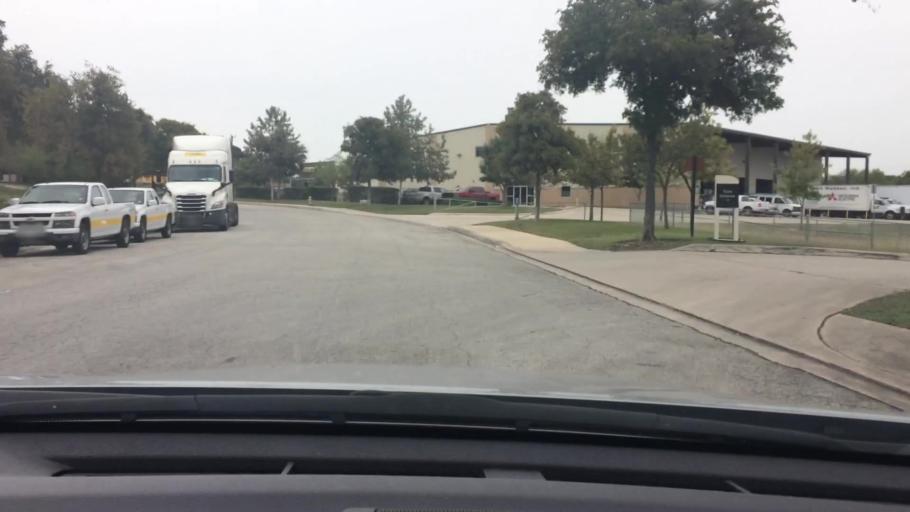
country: US
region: Texas
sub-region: Bexar County
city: Windcrest
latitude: 29.5405
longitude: -98.3722
